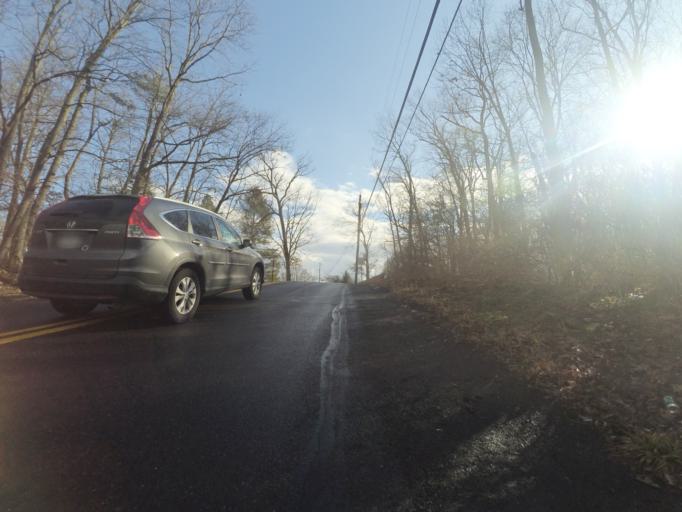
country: US
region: Pennsylvania
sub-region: Centre County
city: Lemont
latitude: 40.8068
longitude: -77.8313
